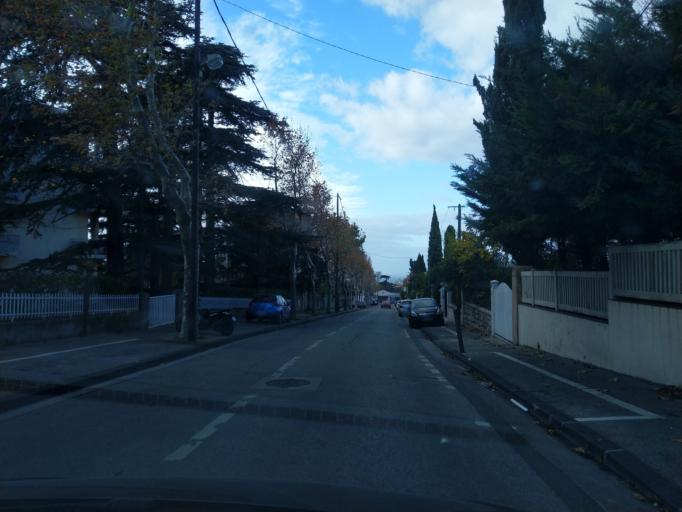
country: FR
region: Provence-Alpes-Cote d'Azur
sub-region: Departement des Bouches-du-Rhone
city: Marseille 13
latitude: 43.3177
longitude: 5.4267
